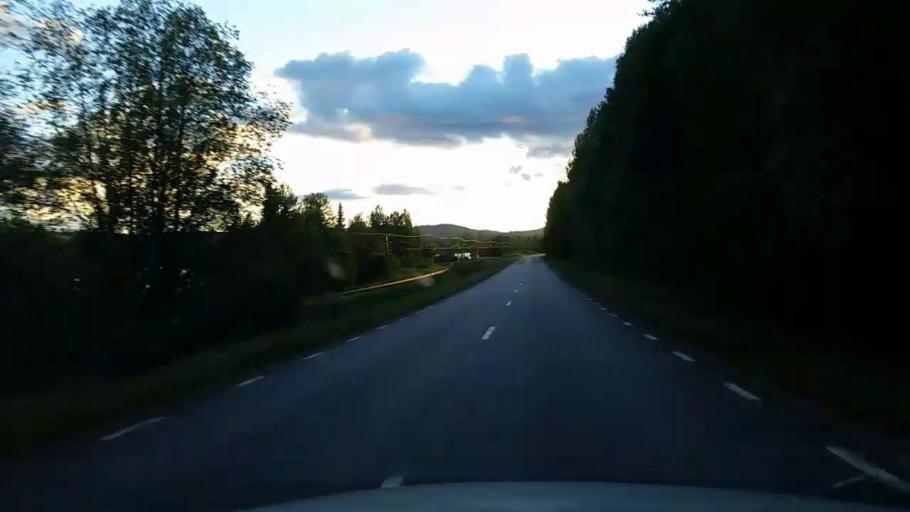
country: SE
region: Gaevleborg
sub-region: Ljusdals Kommun
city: Farila
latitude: 62.1293
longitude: 15.7050
